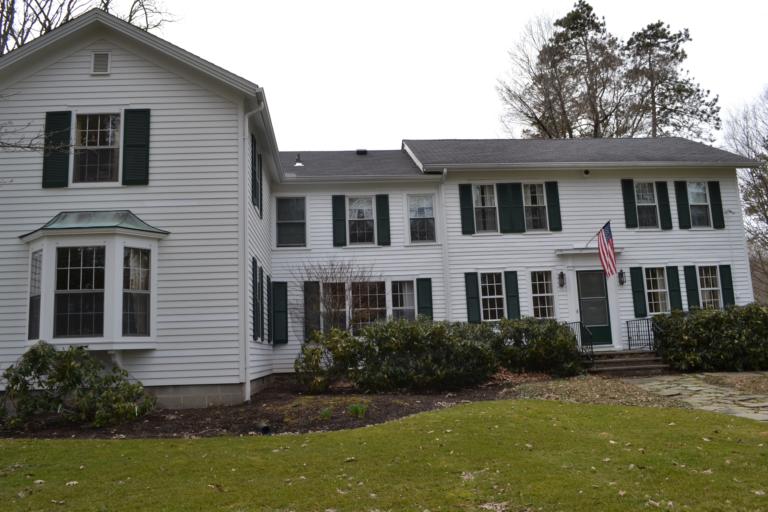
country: US
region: New York
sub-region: Erie County
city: East Aurora
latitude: 42.7083
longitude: -78.5833
